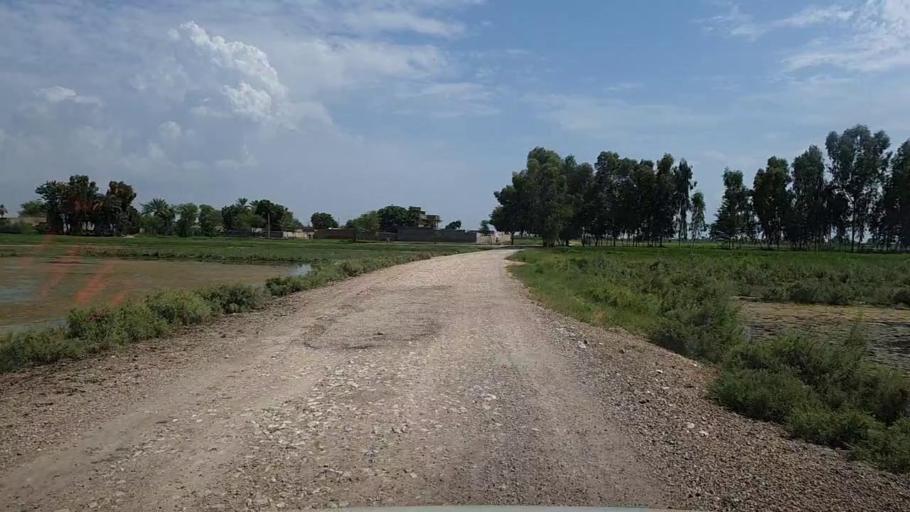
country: PK
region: Sindh
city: Bhiria
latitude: 26.9480
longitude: 68.2431
